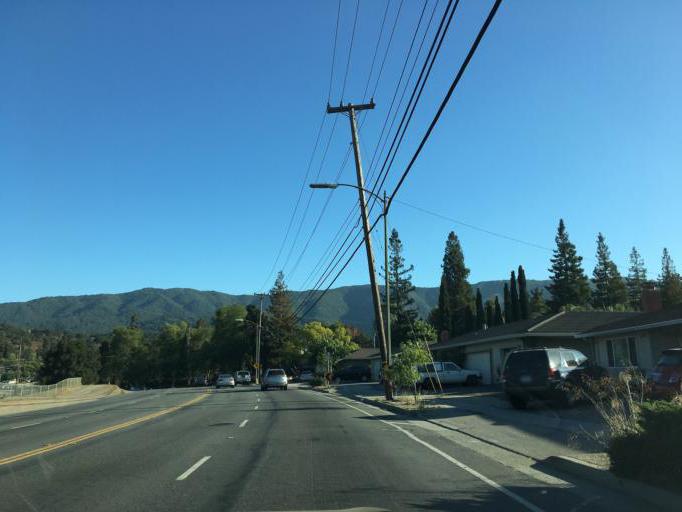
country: US
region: California
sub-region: Santa Clara County
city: Cambrian Park
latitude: 37.2300
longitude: -121.9045
